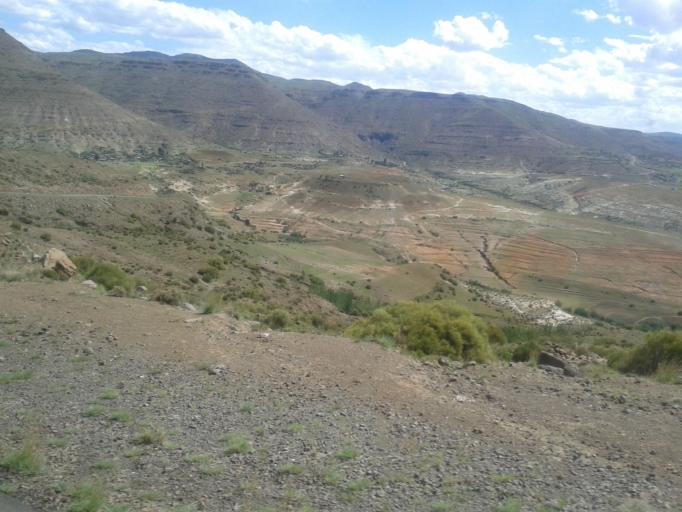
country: LS
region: Qacha's Nek
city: Qacha's Nek
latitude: -30.0462
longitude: 28.3083
